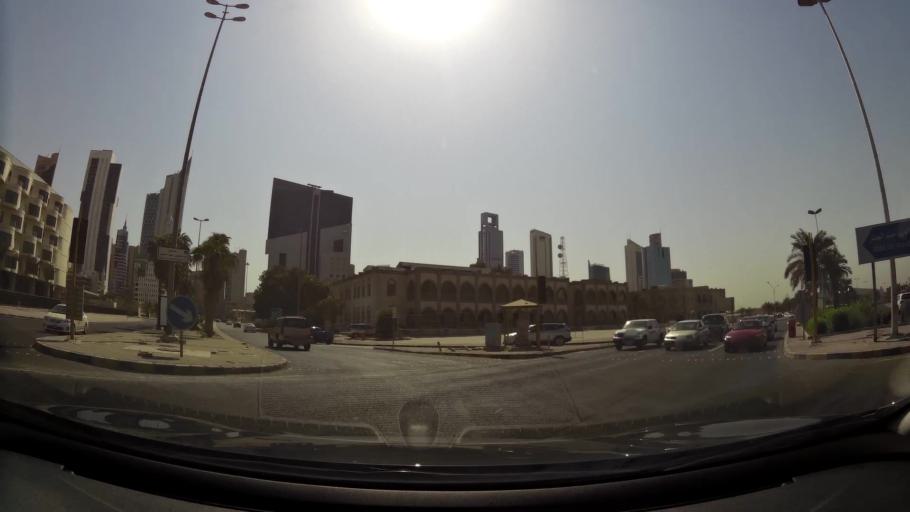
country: KW
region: Al Asimah
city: Kuwait City
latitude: 29.3686
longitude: 47.9621
